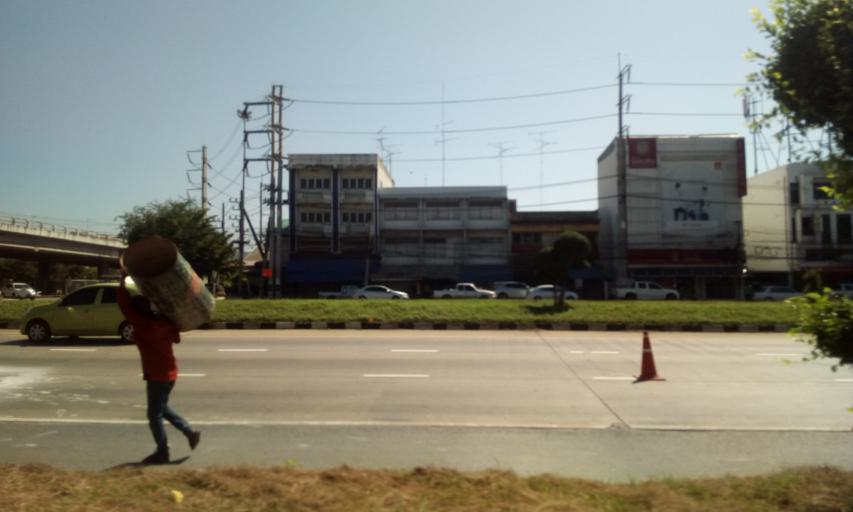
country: TH
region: Sara Buri
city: Nong Khae
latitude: 14.4026
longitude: 100.8898
